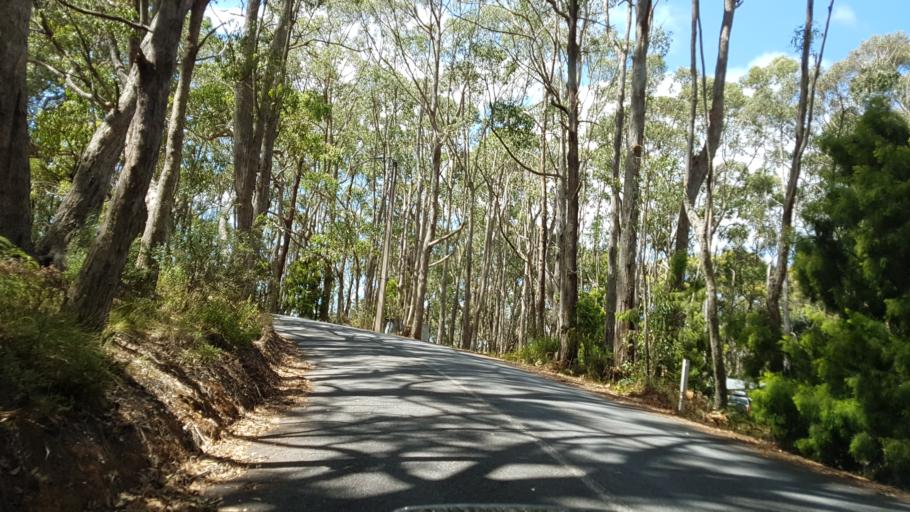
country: AU
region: South Australia
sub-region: Adelaide Hills
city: Crafers
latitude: -34.9714
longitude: 138.7180
